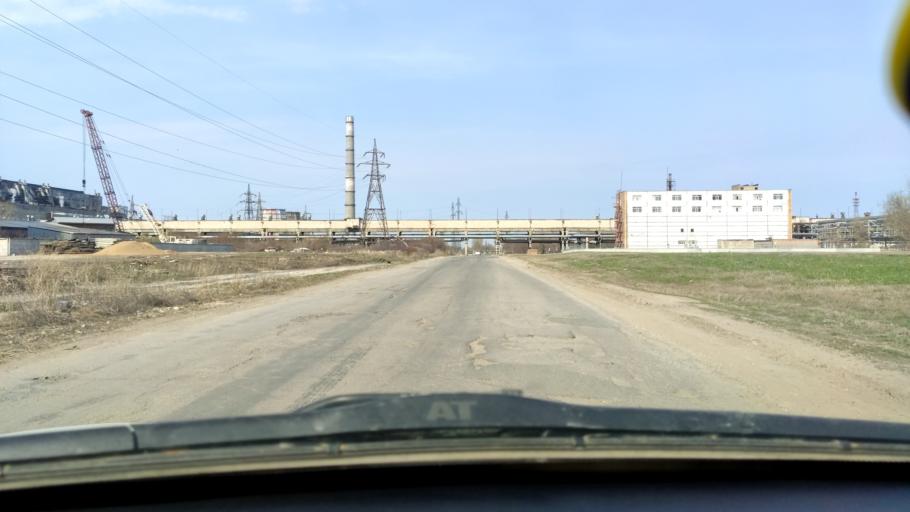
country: RU
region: Samara
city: Tol'yatti
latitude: 53.5491
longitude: 49.4608
